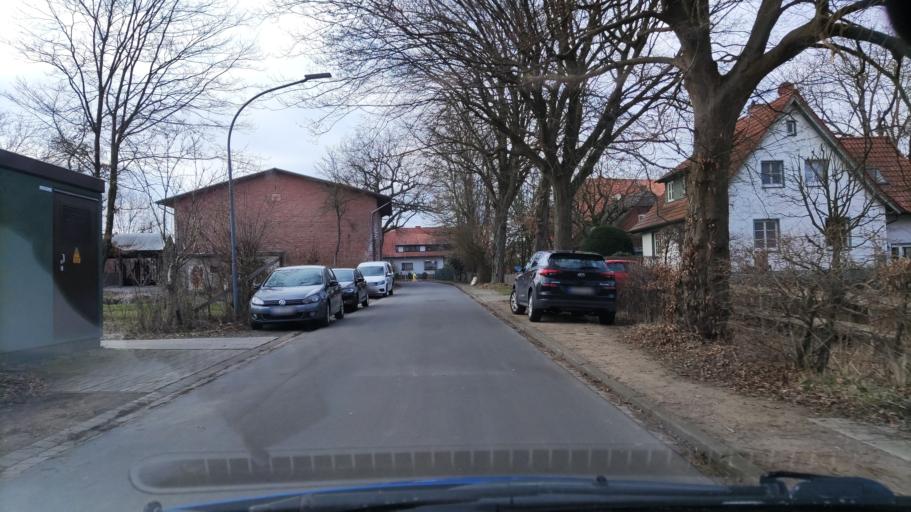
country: DE
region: Lower Saxony
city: Gerdau
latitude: 52.9644
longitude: 10.4580
